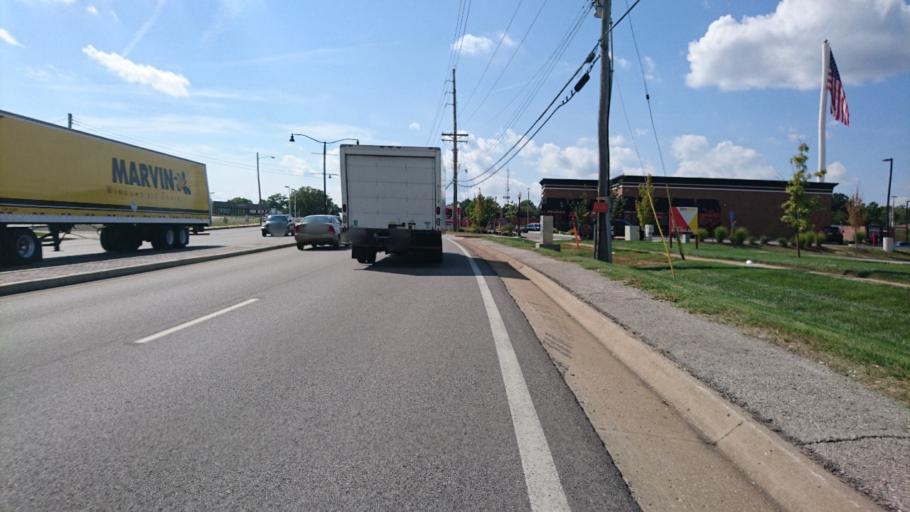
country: US
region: Missouri
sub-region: Saint Louis County
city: Ellisville
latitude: 38.5927
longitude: -90.5874
